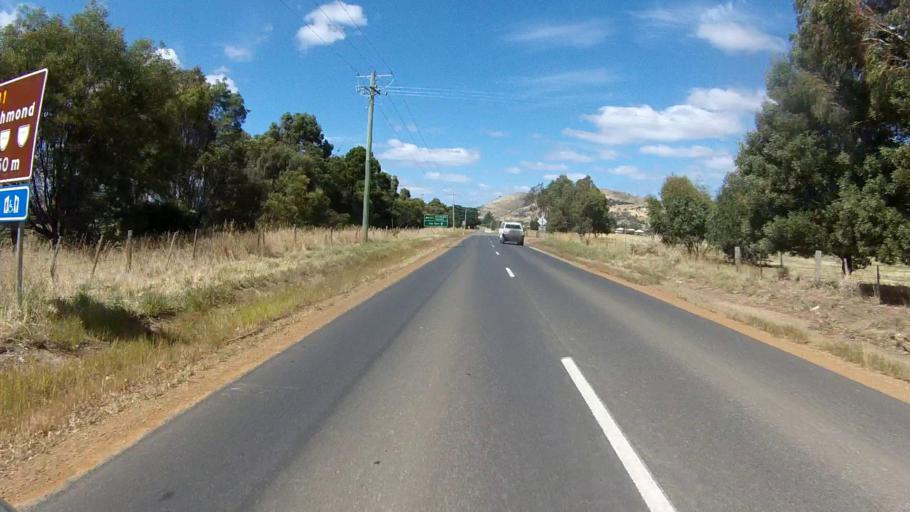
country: AU
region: Tasmania
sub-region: Clarence
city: Cambridge
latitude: -42.7264
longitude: 147.4358
